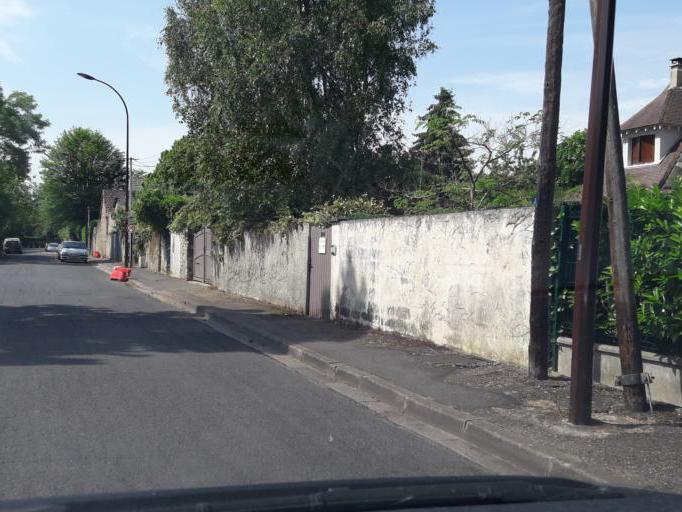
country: FR
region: Ile-de-France
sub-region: Departement de l'Essonne
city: Morsang-sur-Orge
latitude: 48.6515
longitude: 2.3457
